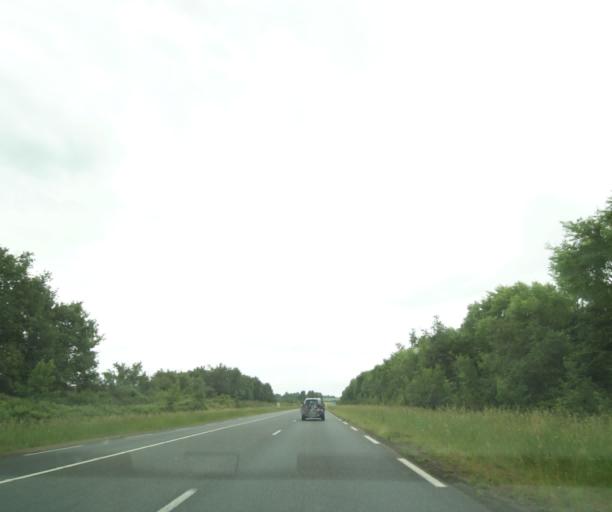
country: FR
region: Poitou-Charentes
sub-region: Departement des Deux-Sevres
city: Airvault
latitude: 46.8059
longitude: -0.2117
